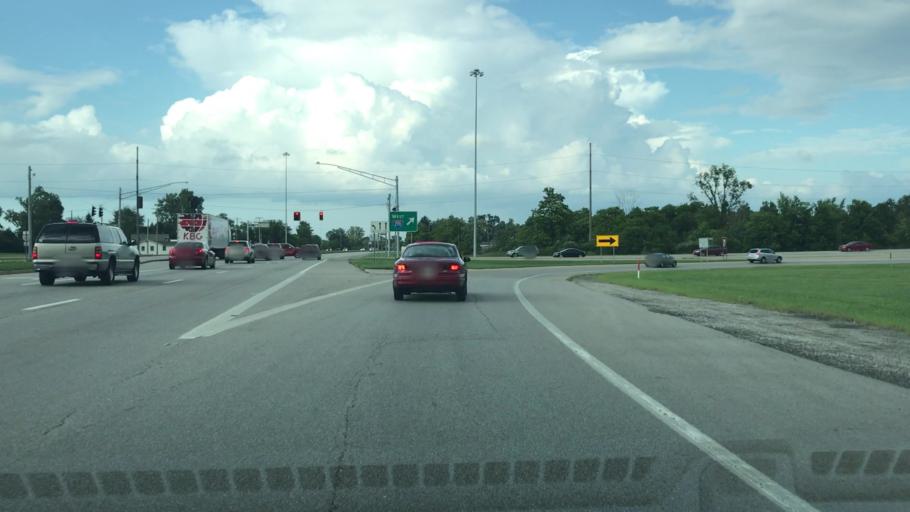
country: US
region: Ohio
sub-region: Franklin County
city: Grove City
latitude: 39.9045
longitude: -83.0752
